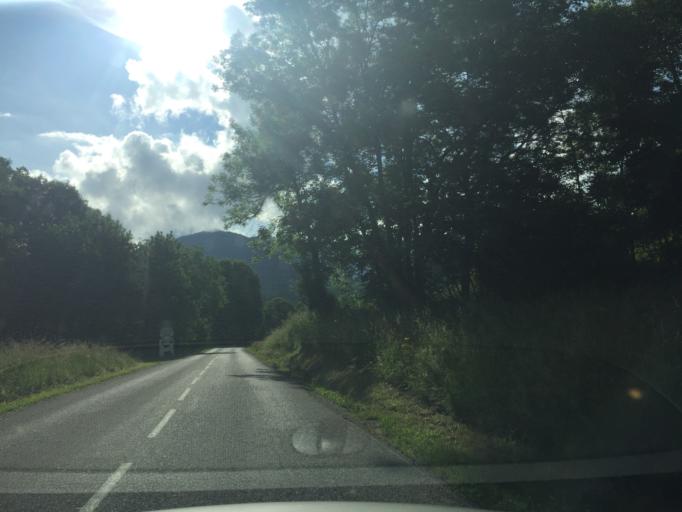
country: FR
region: Rhone-Alpes
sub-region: Departement de la Savoie
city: La Rochette
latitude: 45.4484
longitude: 6.1183
